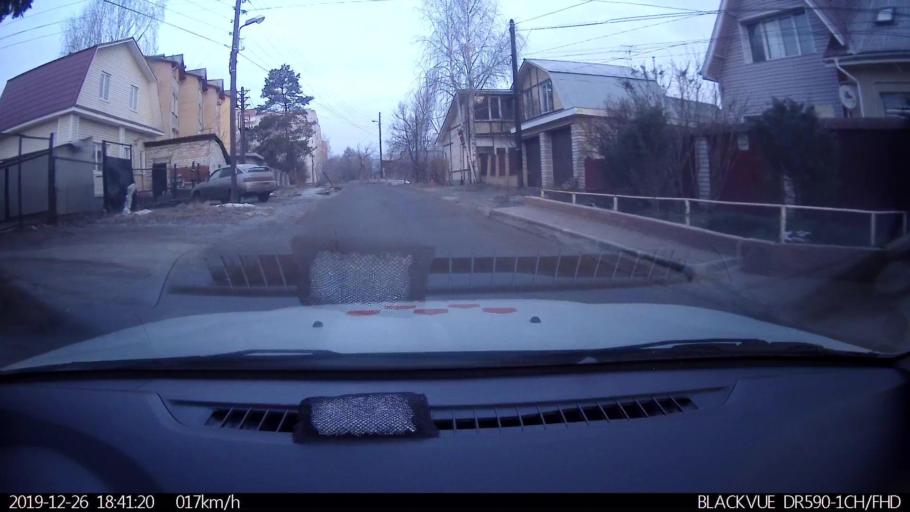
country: RU
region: Nizjnij Novgorod
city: Nizhniy Novgorod
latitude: 56.3156
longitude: 44.0355
